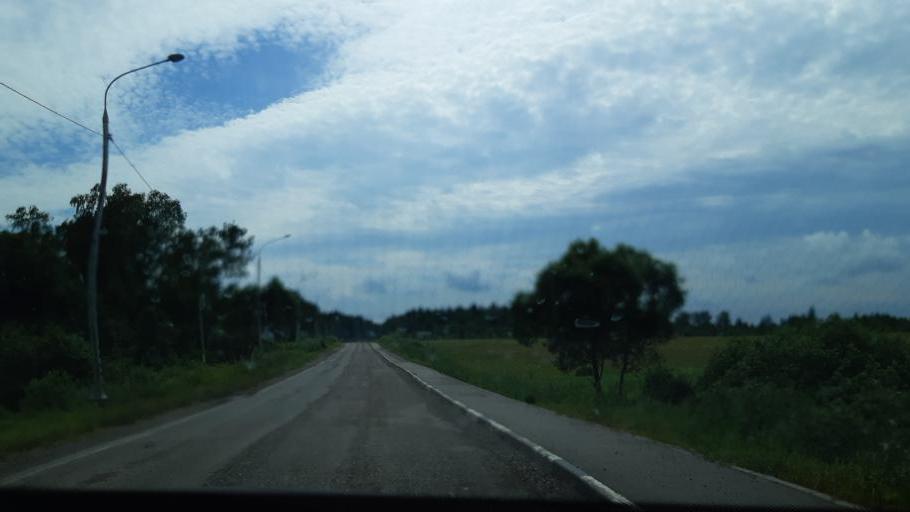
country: RU
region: Moskovskaya
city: Vereya
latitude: 55.2421
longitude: 36.0434
